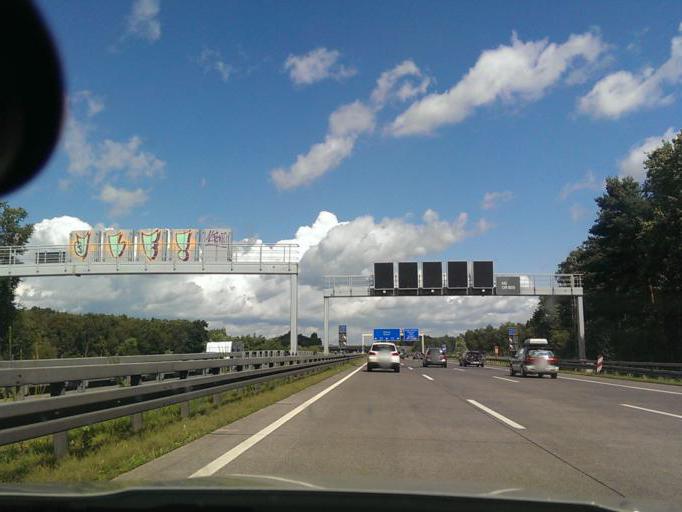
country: DE
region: Lower Saxony
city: Isernhagen Farster Bauerschaft
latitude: 52.4200
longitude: 9.8921
